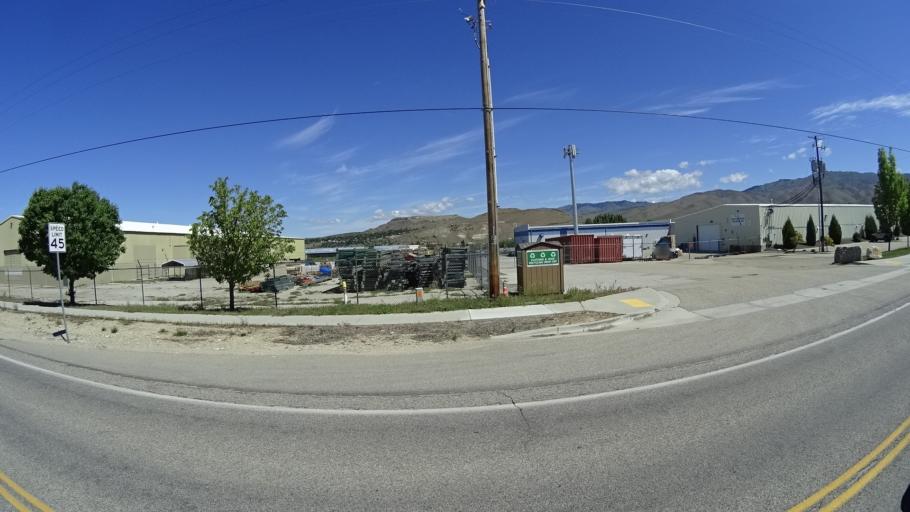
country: US
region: Idaho
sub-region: Ada County
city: Boise
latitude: 43.5605
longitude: -116.1424
